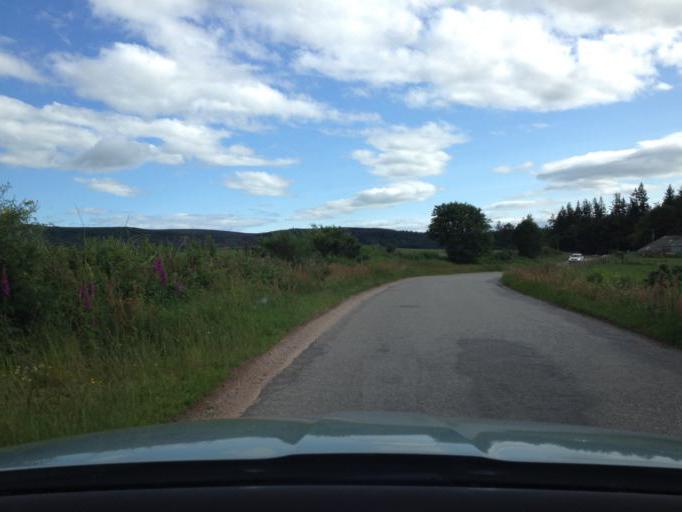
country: GB
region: Scotland
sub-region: Aberdeenshire
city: Banchory
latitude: 56.9807
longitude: -2.5730
